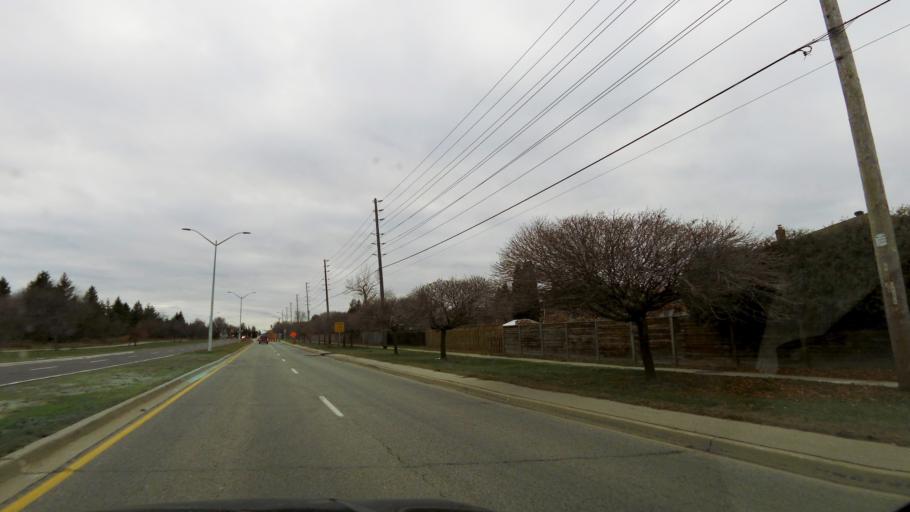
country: CA
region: Ontario
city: Mississauga
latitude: 43.5632
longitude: -79.6199
